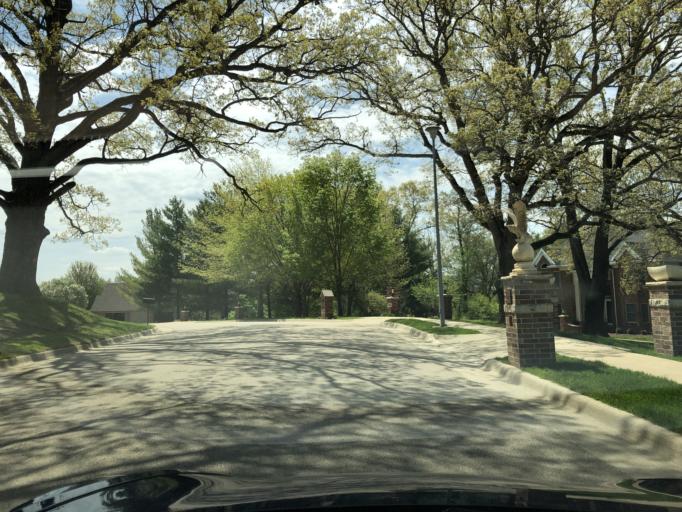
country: US
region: Iowa
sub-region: Dubuque County
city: Dubuque
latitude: 42.4757
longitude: -90.6630
